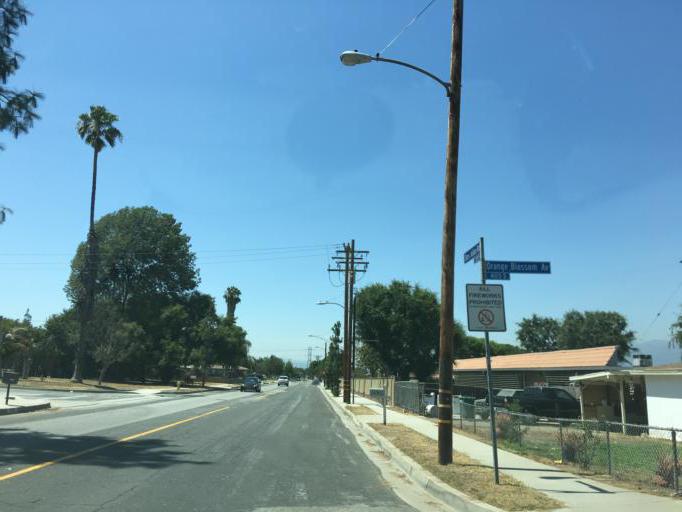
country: US
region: California
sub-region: Los Angeles County
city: Avocado Heights
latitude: 34.0422
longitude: -117.9995
